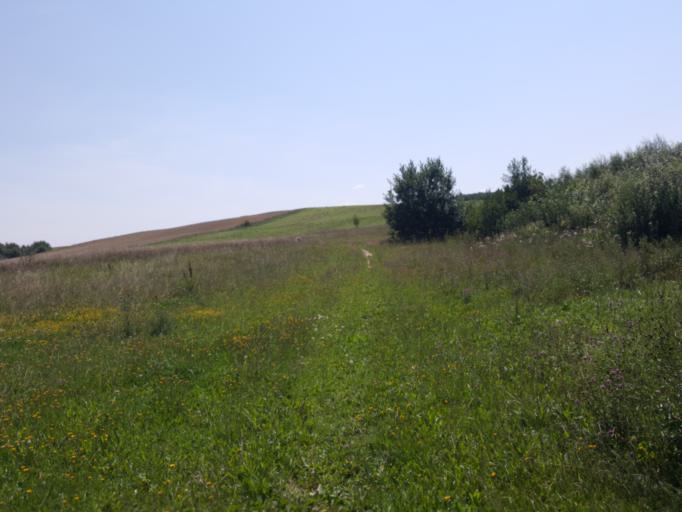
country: LT
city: Vilkaviskis
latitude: 54.4392
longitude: 22.9877
